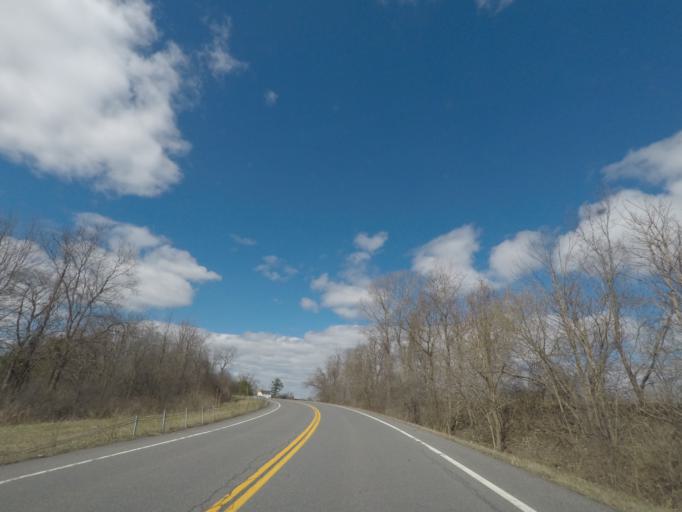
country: US
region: New York
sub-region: Albany County
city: Delmar
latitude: 42.5633
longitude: -73.8238
